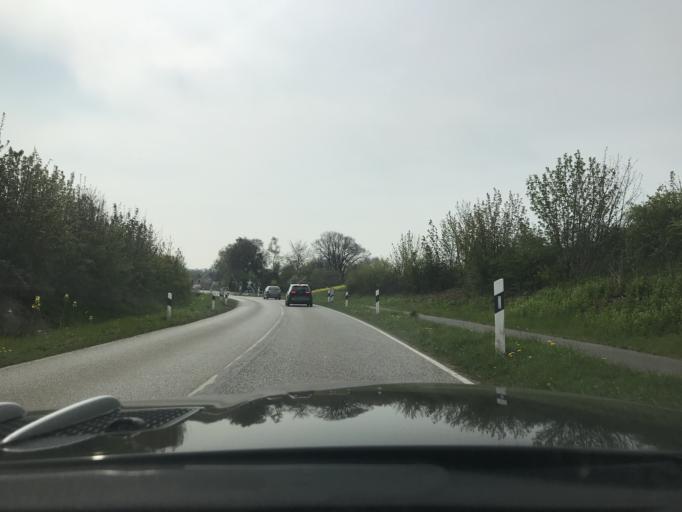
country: DE
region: Schleswig-Holstein
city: Heringsdorf
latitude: 54.3046
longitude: 11.0059
